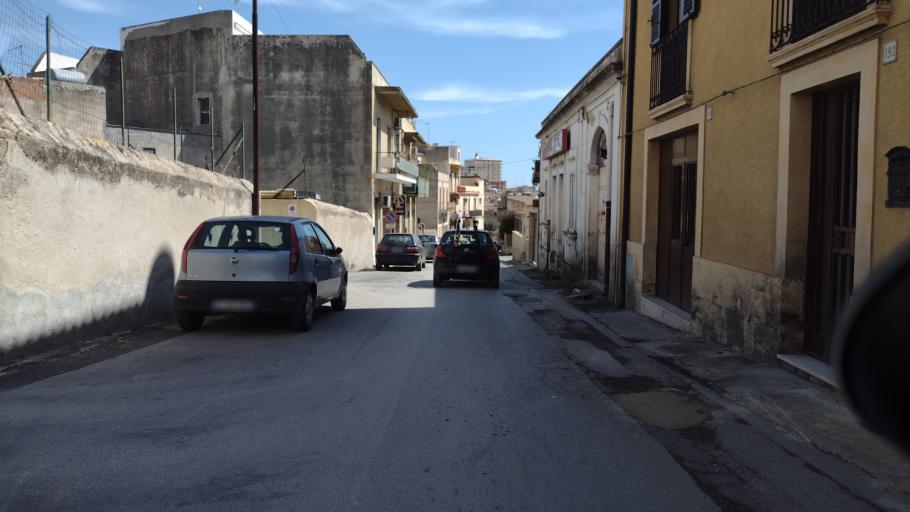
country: IT
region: Sicily
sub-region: Provincia di Siracusa
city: Noto
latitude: 36.8891
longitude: 15.0687
